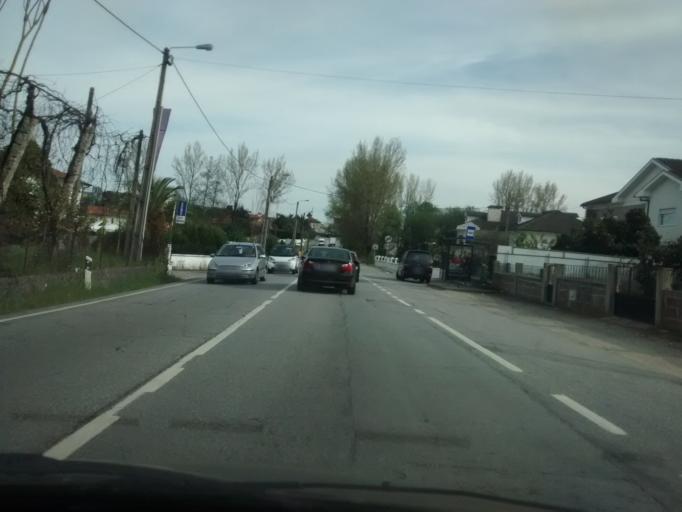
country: PT
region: Braga
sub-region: Guimaraes
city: Brito
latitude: 41.4907
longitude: -8.3599
